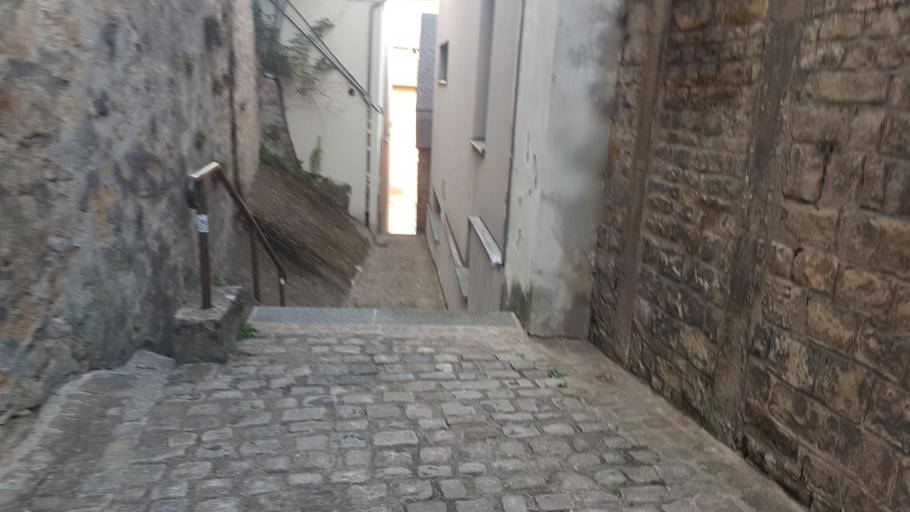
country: LU
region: Luxembourg
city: Kirchberg
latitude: 49.6133
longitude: 6.1426
